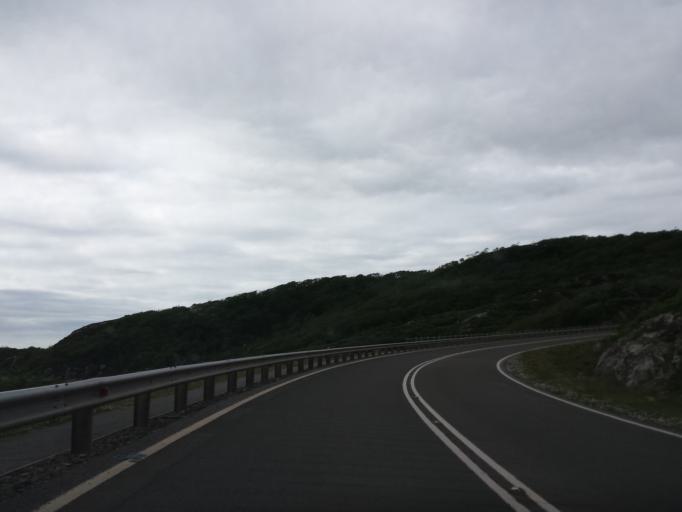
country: GB
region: Scotland
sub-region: Argyll and Bute
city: Isle Of Mull
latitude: 56.8937
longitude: -5.7566
